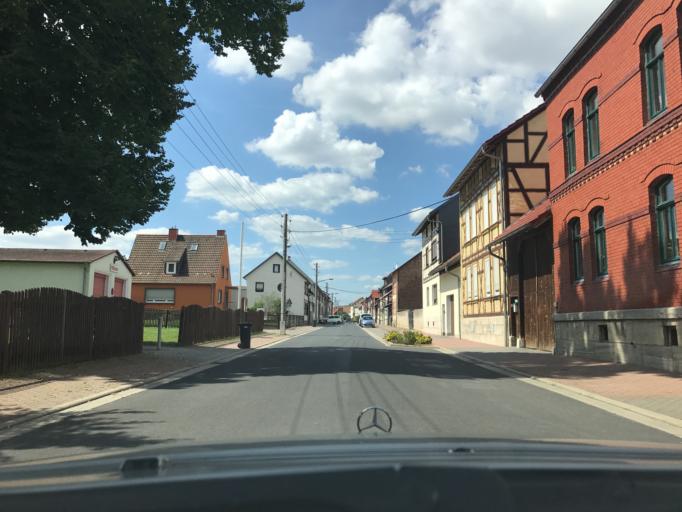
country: DE
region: Thuringia
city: Muehlhausen
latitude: 51.2106
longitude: 10.4926
